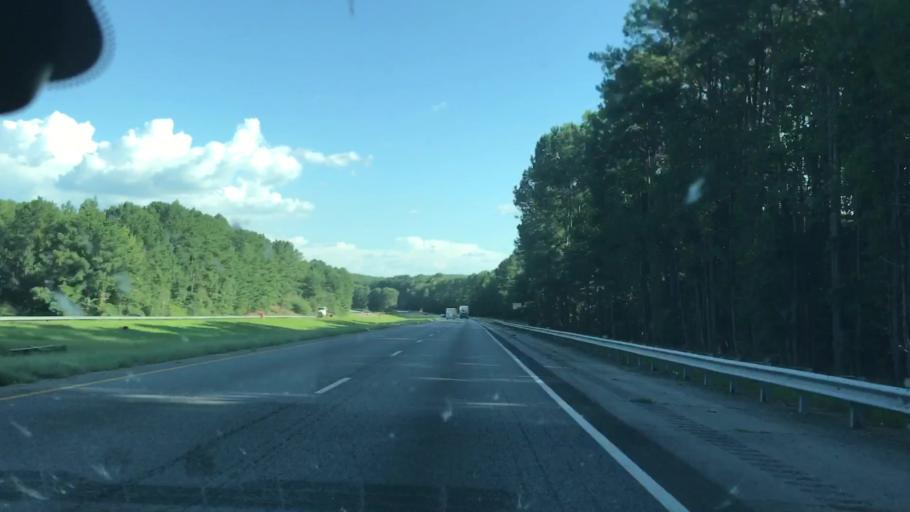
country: US
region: Georgia
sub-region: Harris County
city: Hamilton
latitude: 32.6433
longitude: -84.9706
